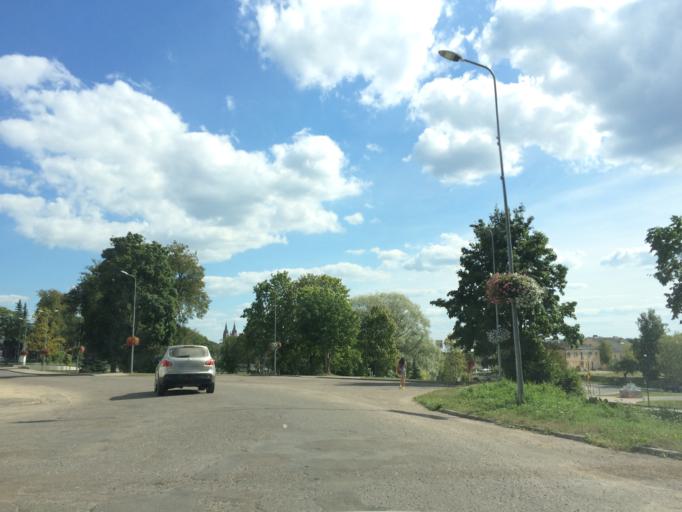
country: LV
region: Rezekne
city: Rezekne
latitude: 56.5053
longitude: 27.3271
